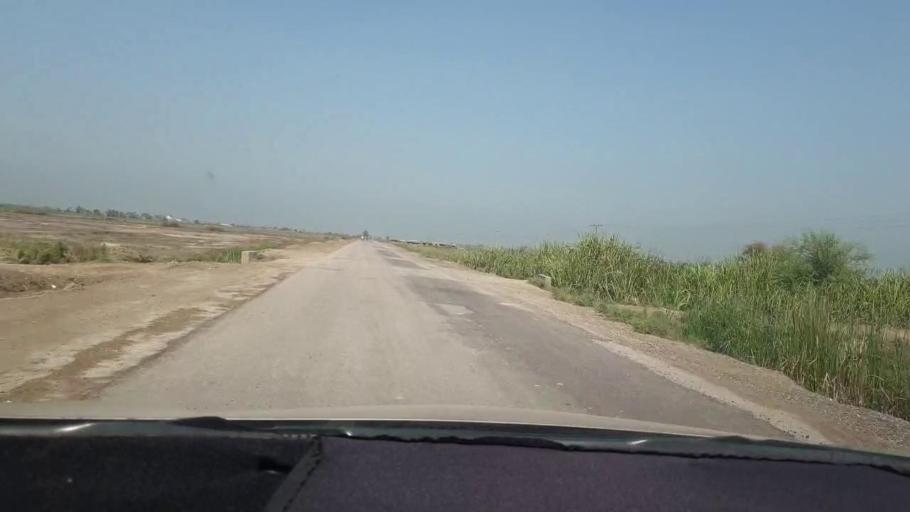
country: PK
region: Sindh
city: Miro Khan
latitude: 27.8316
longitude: 68.0144
